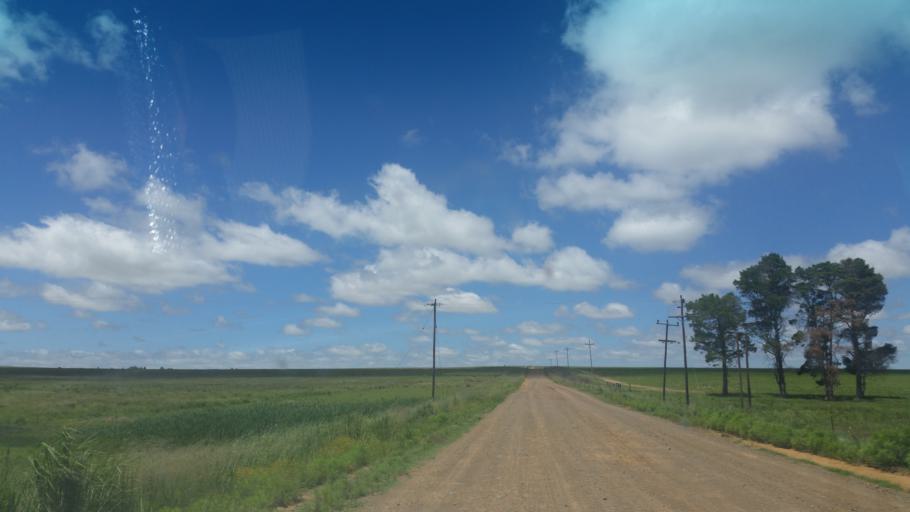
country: ZA
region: Orange Free State
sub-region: Thabo Mofutsanyana District Municipality
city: Harrismith
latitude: -28.1889
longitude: 28.9952
